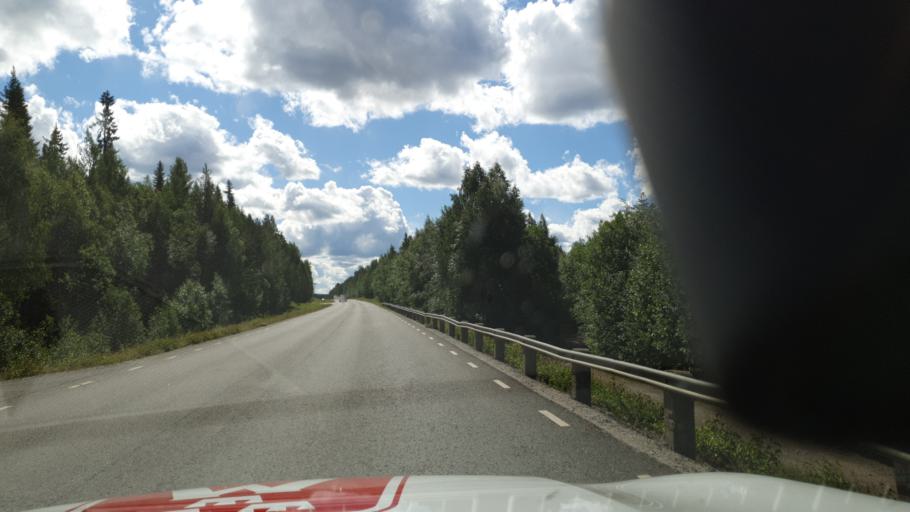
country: SE
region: Vaesterbotten
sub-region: Lycksele Kommun
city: Lycksele
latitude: 64.6206
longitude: 18.6861
